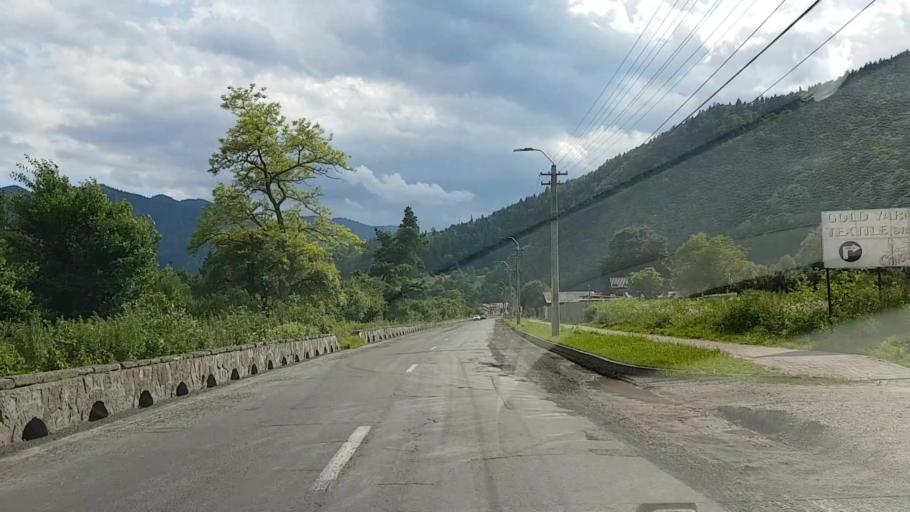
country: RO
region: Neamt
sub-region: Comuna Bicaz
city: Dodeni
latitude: 46.9238
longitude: 26.0921
